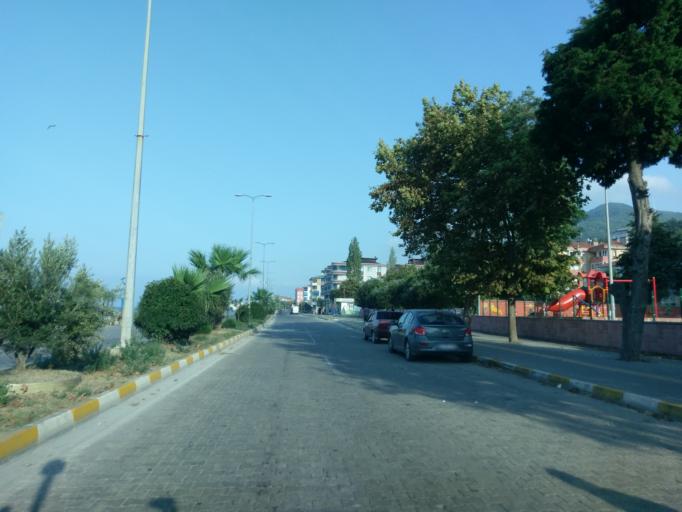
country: TR
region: Kastamonu
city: Catalzeytin
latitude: 41.9541
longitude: 34.2170
